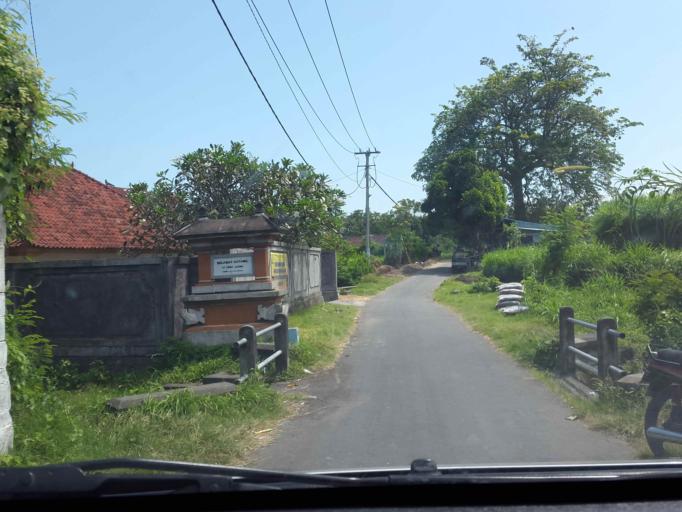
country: ID
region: Bali
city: Semarapura
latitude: -8.5572
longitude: 115.3991
